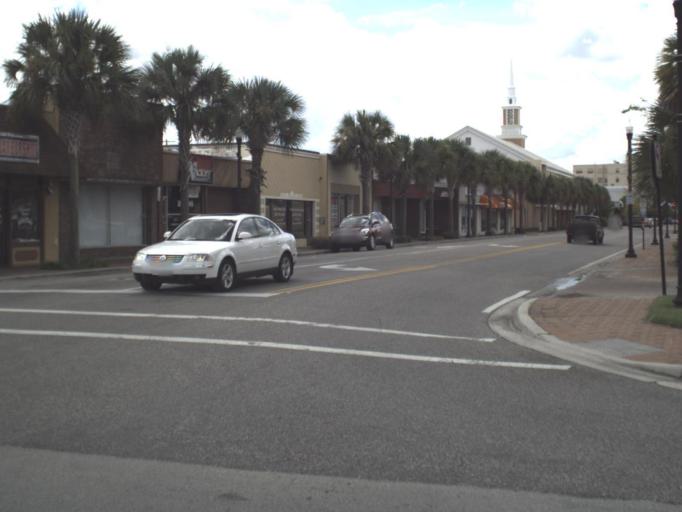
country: US
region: Florida
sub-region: Polk County
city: Winter Haven
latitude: 28.0222
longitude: -81.7269
